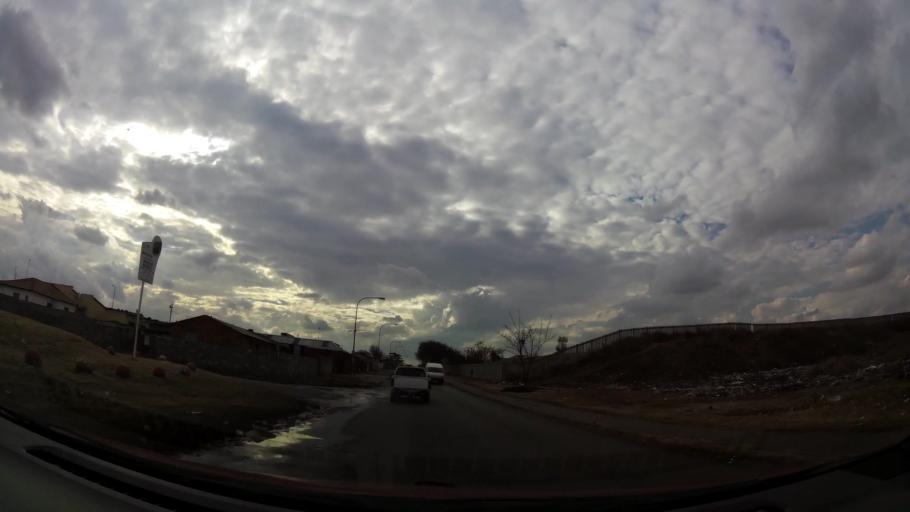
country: ZA
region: Gauteng
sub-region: City of Johannesburg Metropolitan Municipality
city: Soweto
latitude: -26.2449
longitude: 27.8403
